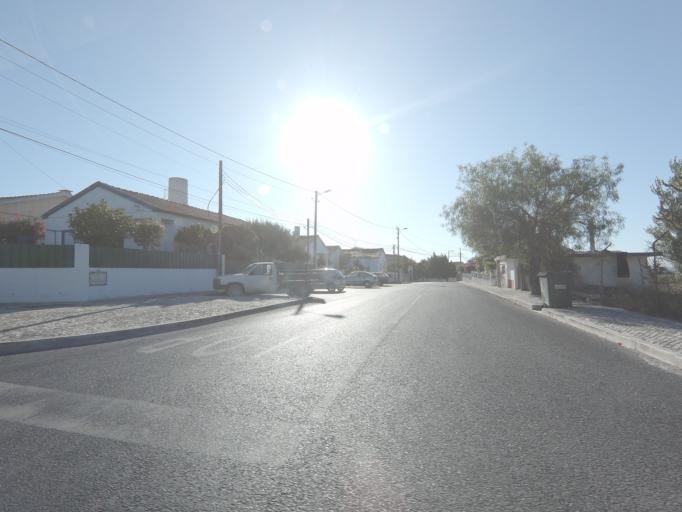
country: PT
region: Setubal
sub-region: Palmela
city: Quinta do Anjo
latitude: 38.5344
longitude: -8.9884
